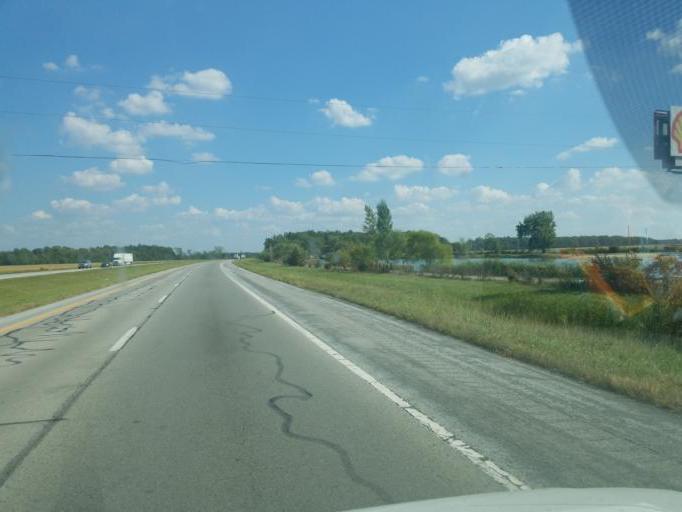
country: US
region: Ohio
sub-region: Allen County
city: Elida
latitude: 40.8344
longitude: -84.1664
